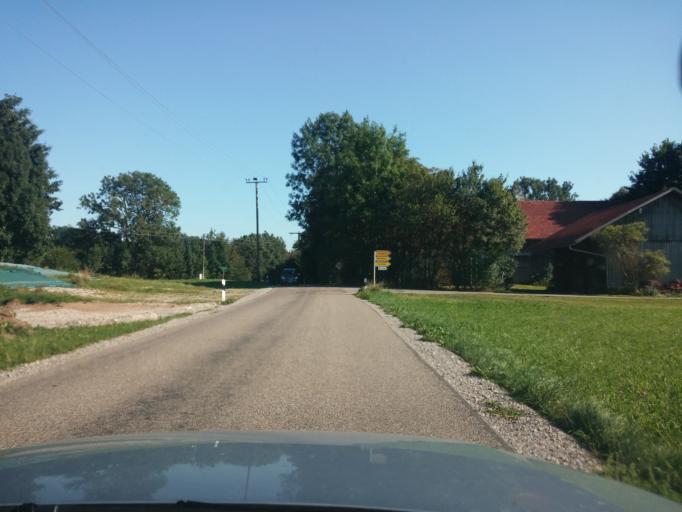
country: DE
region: Bavaria
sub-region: Swabia
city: Altusried
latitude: 47.8294
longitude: 10.1747
